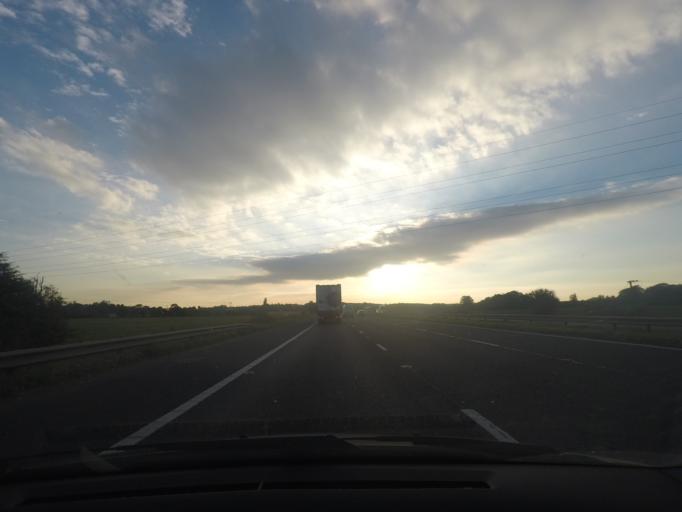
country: GB
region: England
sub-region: North Lincolnshire
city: Brigg
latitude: 53.5562
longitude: -0.5072
